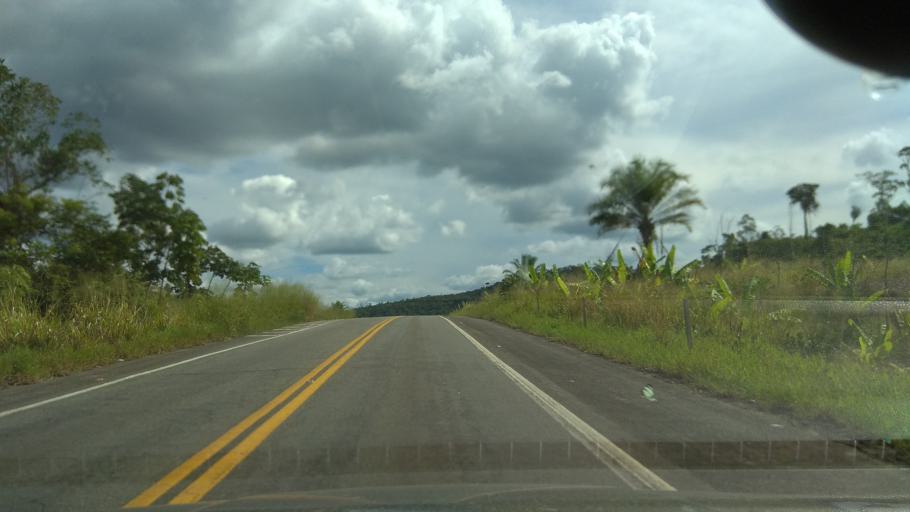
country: BR
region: Bahia
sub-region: Ubaitaba
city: Ubaitaba
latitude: -14.2519
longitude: -39.3687
